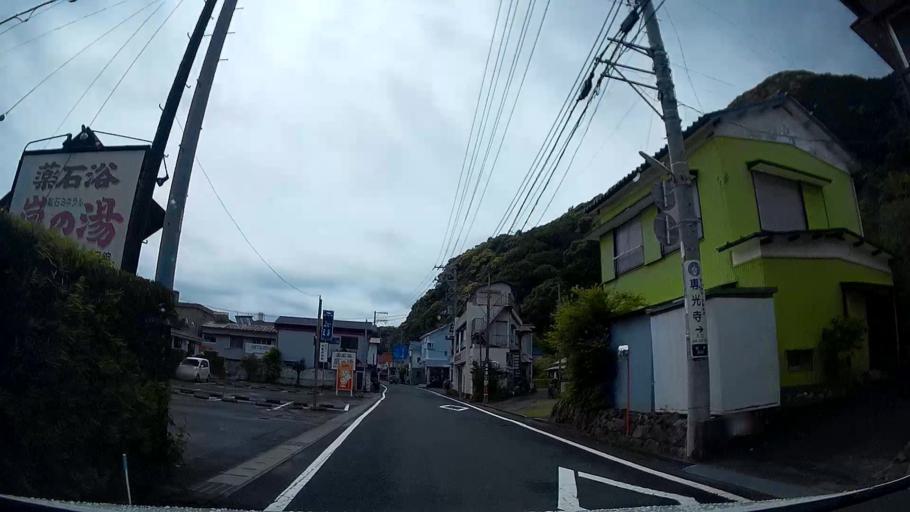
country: JP
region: Shizuoka
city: Shimoda
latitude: 34.7444
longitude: 138.9947
